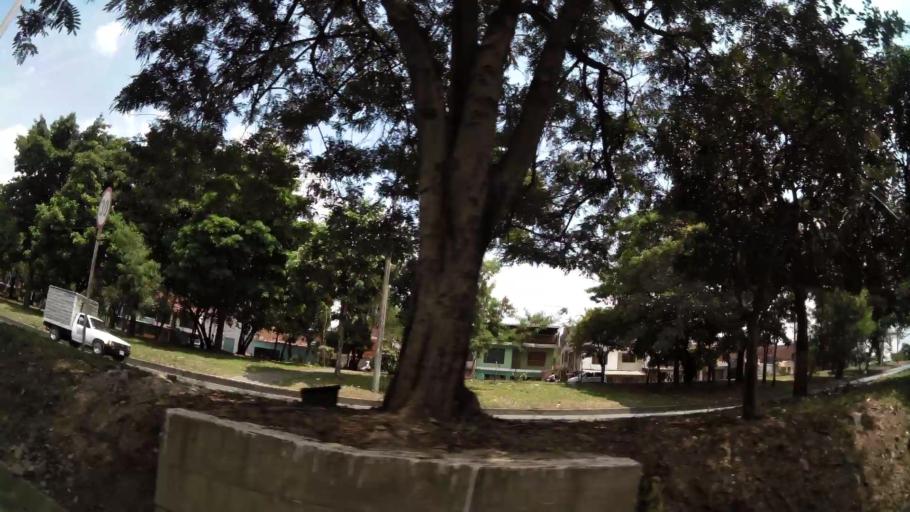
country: CO
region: Valle del Cauca
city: Cali
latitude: 3.4718
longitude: -76.4822
